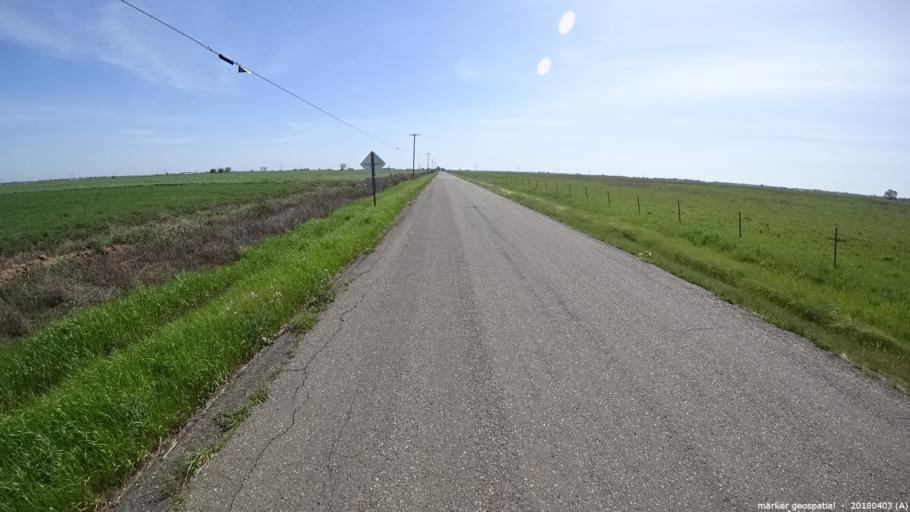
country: US
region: California
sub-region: Sacramento County
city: Wilton
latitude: 38.3701
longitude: -121.2975
